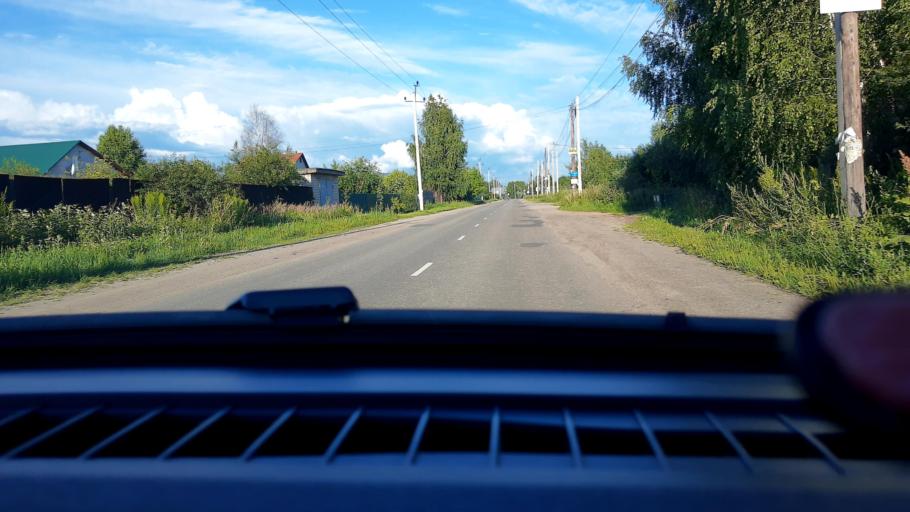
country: RU
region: Nizjnij Novgorod
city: Bor
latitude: 56.3526
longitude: 44.1198
